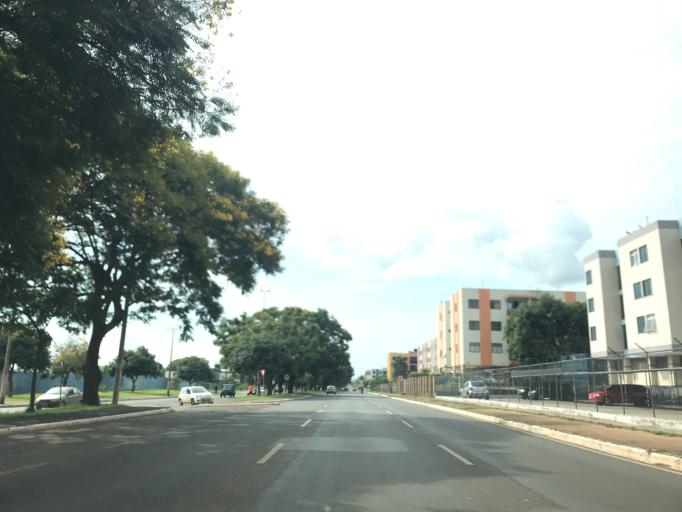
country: BR
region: Federal District
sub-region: Brasilia
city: Brasilia
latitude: -15.8163
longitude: -48.0881
